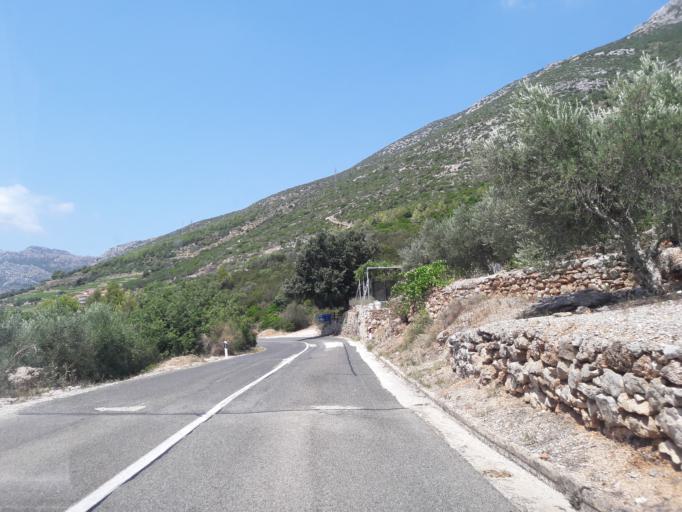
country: HR
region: Dubrovacko-Neretvanska
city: Orebic
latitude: 42.9761
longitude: 17.2304
